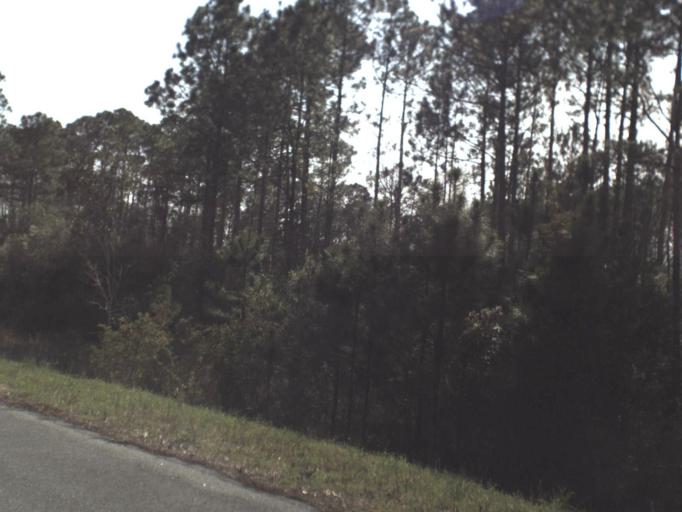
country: US
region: Florida
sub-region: Franklin County
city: Carrabelle
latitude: 29.9555
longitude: -84.5053
